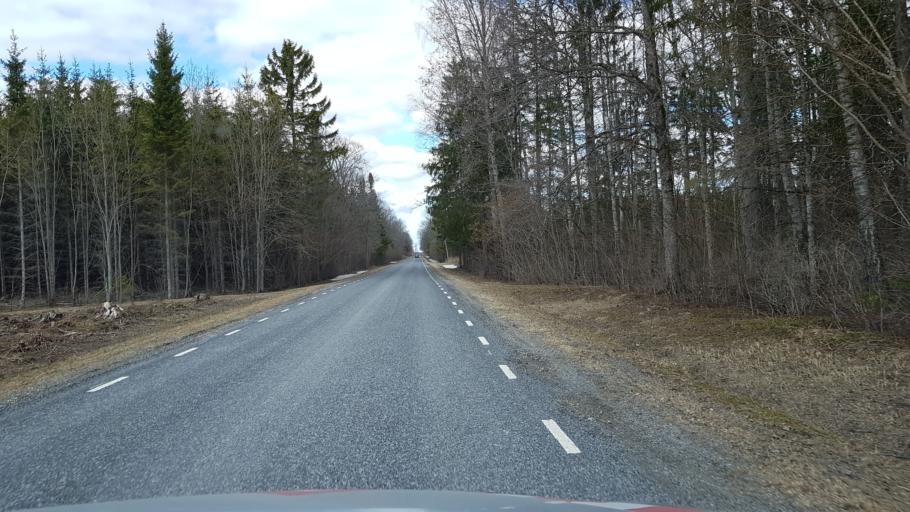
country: EE
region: Laeaene-Virumaa
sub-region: Tamsalu vald
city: Tamsalu
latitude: 59.1944
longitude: 26.1315
